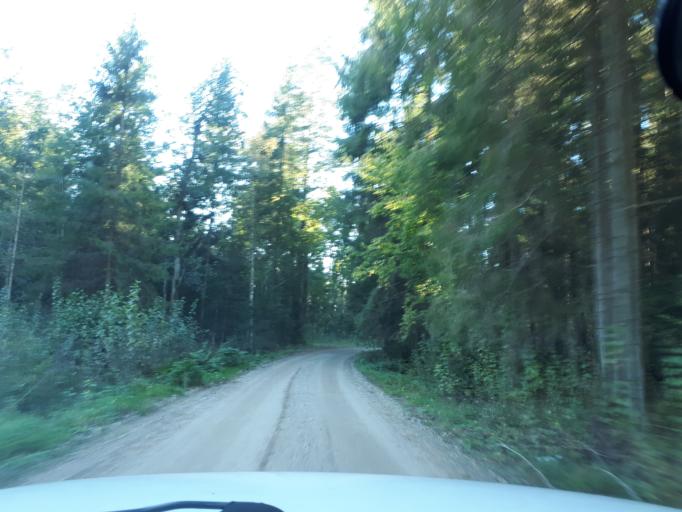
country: LT
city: Kulautuva
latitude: 54.9320
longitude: 23.5848
